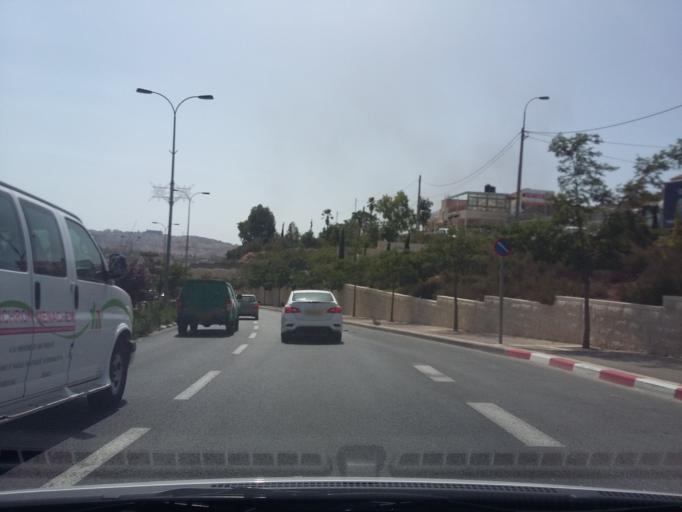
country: PS
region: West Bank
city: Ar Ram wa Dahiyat al Barid
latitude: 31.8298
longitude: 35.2209
